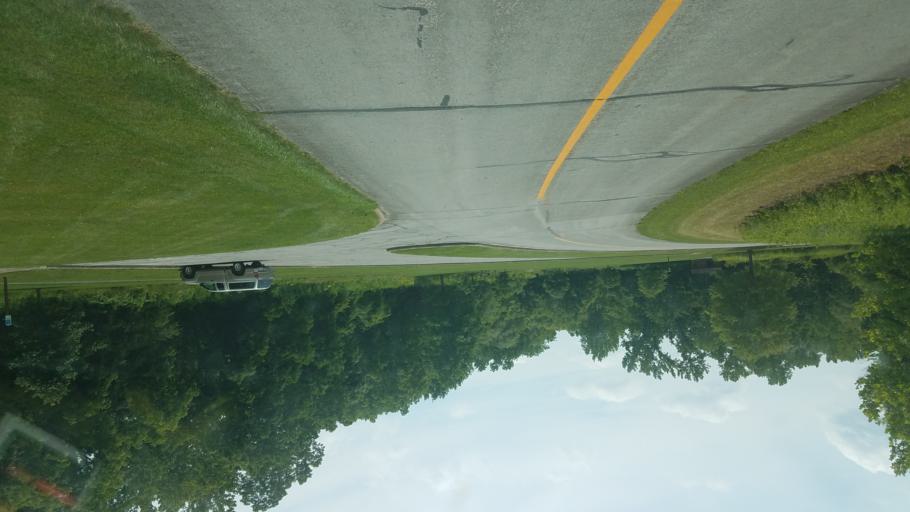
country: US
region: Ohio
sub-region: Delaware County
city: Powell
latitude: 40.1549
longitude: -83.0435
